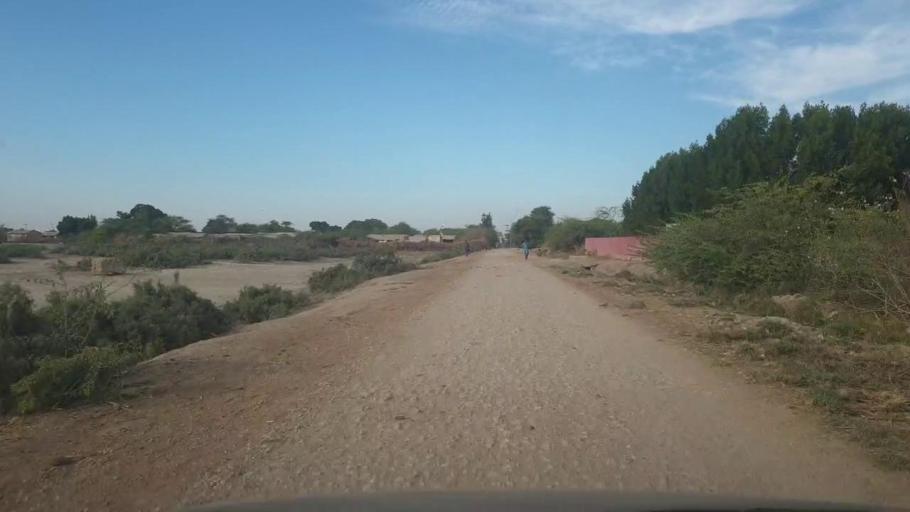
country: PK
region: Sindh
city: Samaro
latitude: 25.3285
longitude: 69.2670
